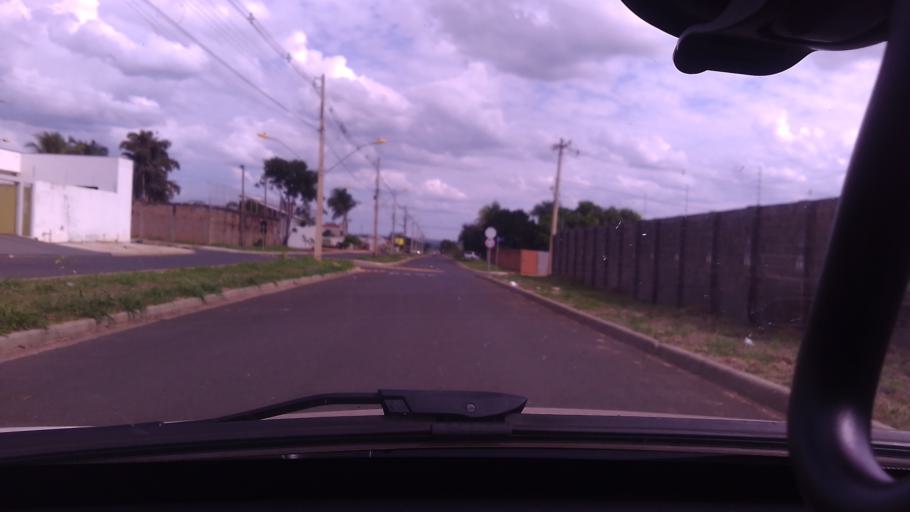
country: BR
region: Goias
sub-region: Mineiros
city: Mineiros
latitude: -17.5767
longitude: -52.5527
